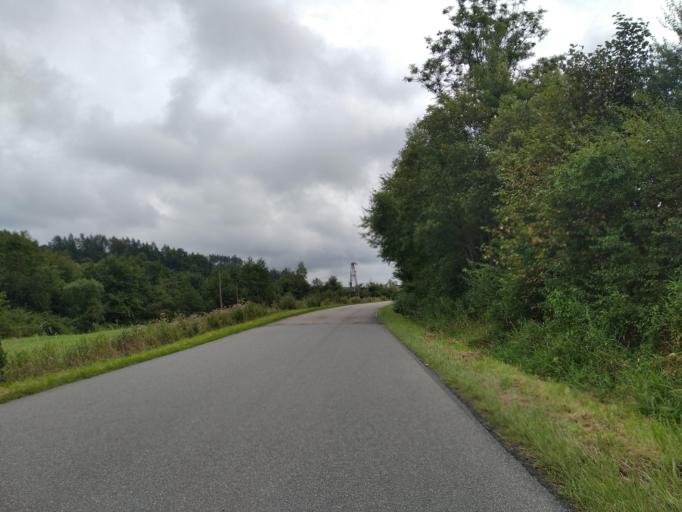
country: PL
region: Subcarpathian Voivodeship
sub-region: Powiat brzozowski
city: Nozdrzec
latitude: 49.7401
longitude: 22.2461
